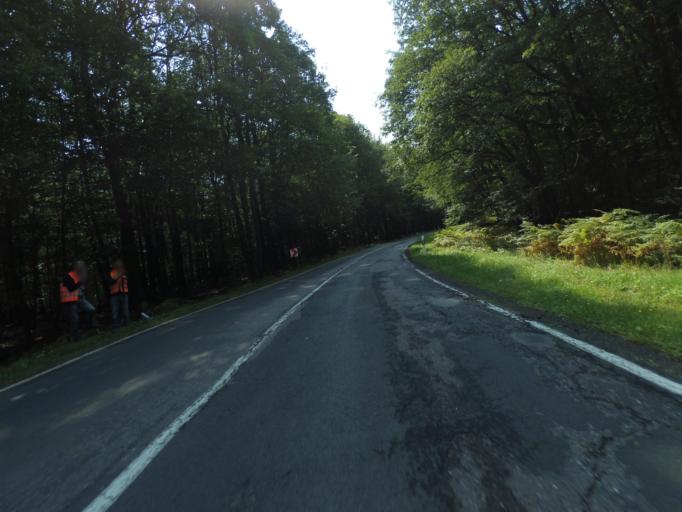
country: DE
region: Saarland
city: Britten
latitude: 49.5128
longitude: 6.6555
